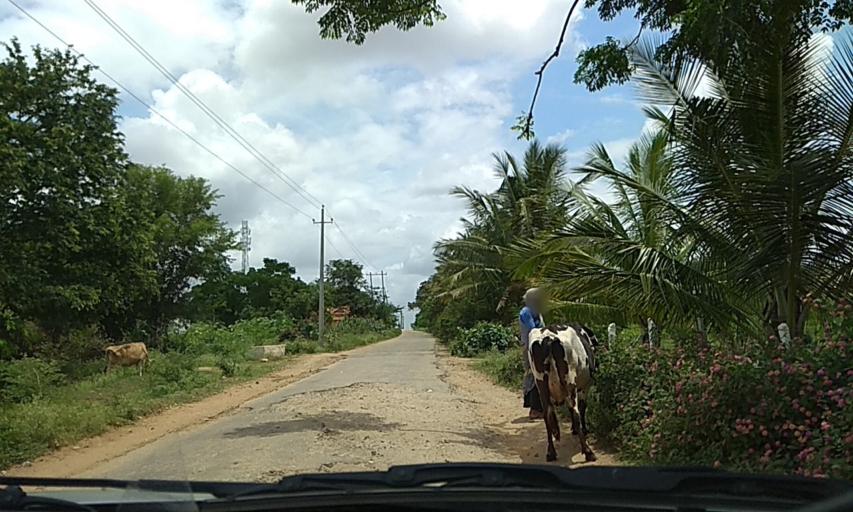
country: IN
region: Karnataka
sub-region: Chamrajnagar
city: Gundlupet
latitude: 11.8877
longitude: 76.6960
